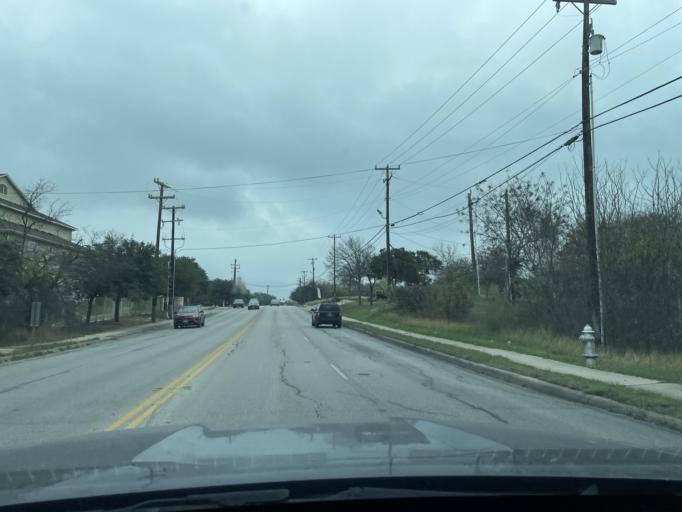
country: US
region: Texas
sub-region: Bexar County
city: Leon Valley
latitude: 29.5572
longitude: -98.6184
